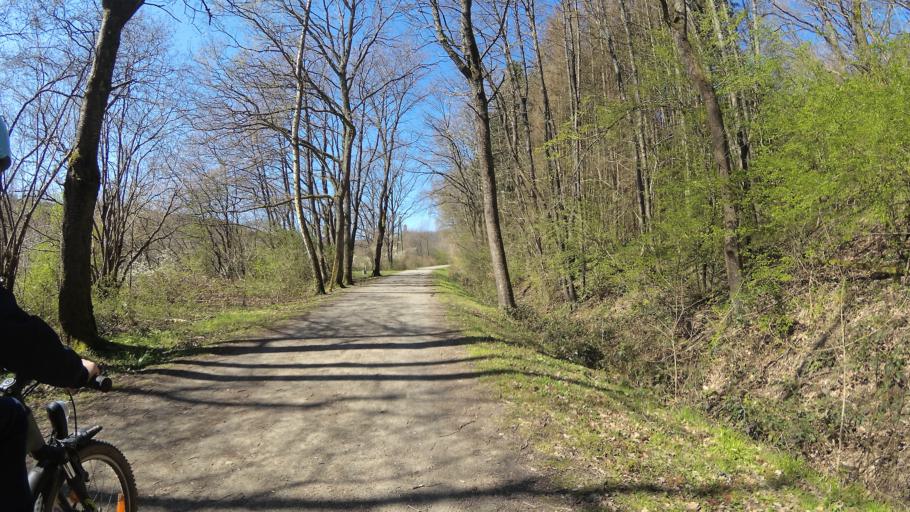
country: DE
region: Rheinland-Pfalz
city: Ruthweiler
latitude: 49.5507
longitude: 7.3739
